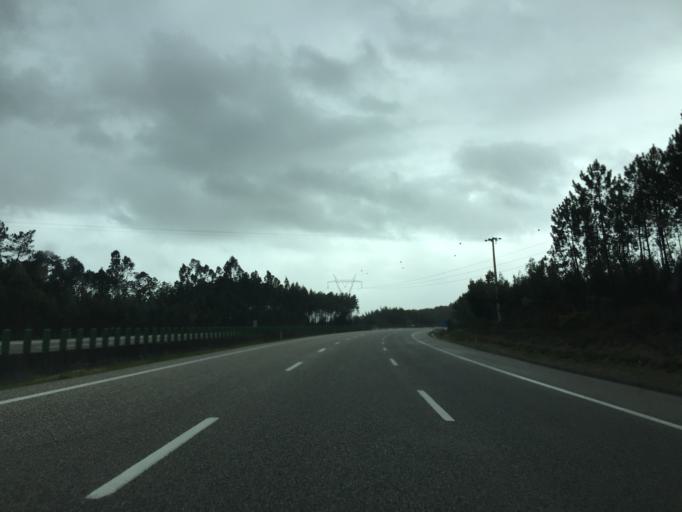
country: PT
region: Leiria
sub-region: Pombal
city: Lourical
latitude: 39.9391
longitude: -8.7704
